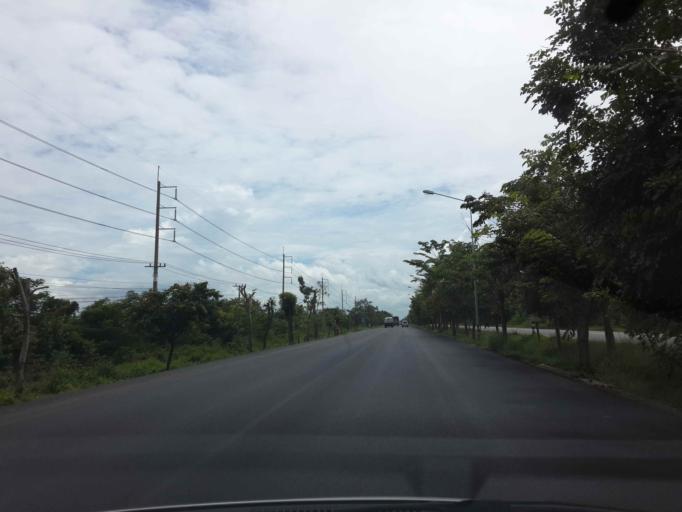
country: TH
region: Ratchaburi
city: Pak Tho
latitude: 13.4262
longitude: 99.8076
